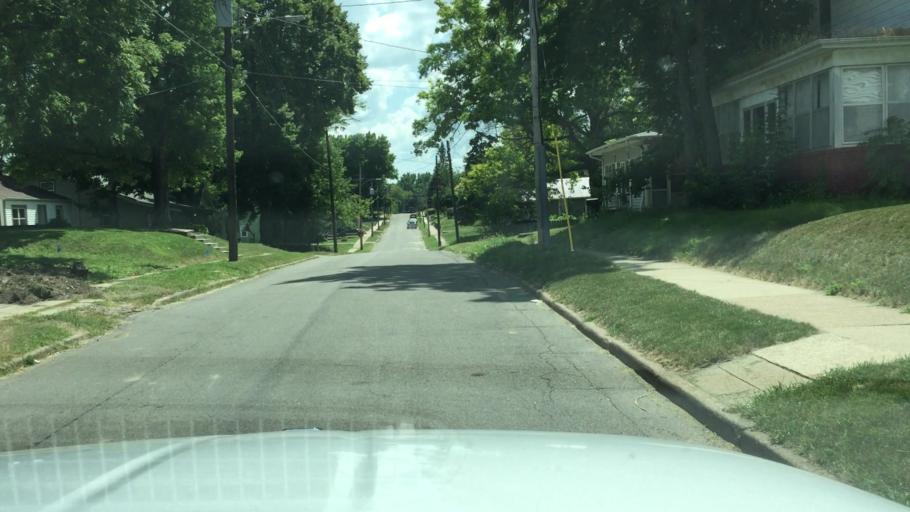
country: US
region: Iowa
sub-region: Jasper County
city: Newton
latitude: 41.6955
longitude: -93.0549
